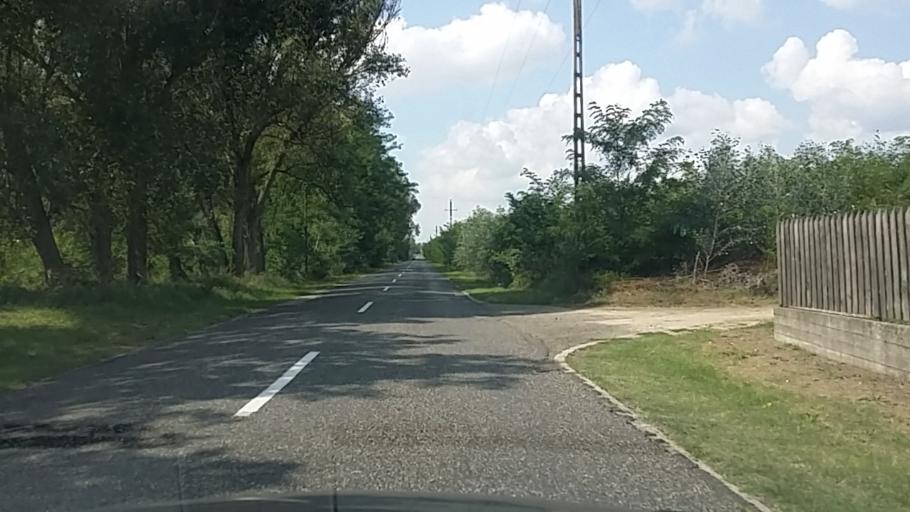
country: HU
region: Bacs-Kiskun
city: Lakitelek
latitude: 46.8616
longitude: 19.9726
